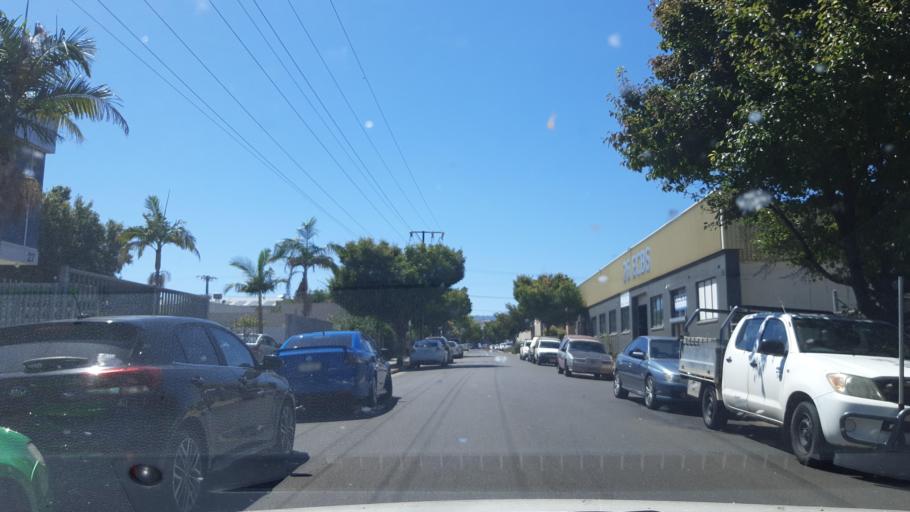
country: AU
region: South Australia
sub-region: Marion
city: Clovelly Park
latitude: -34.9879
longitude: 138.5697
